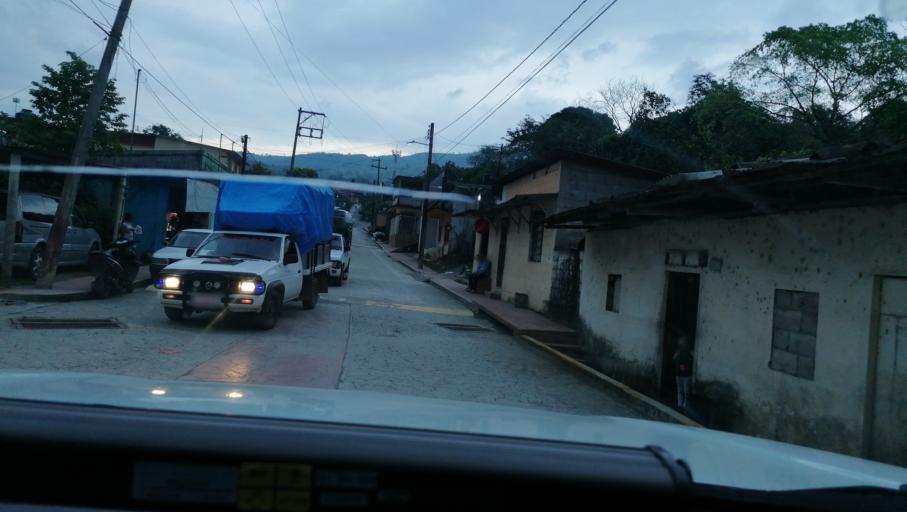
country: MX
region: Chiapas
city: Ixtacomitan
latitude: 17.4284
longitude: -93.1000
